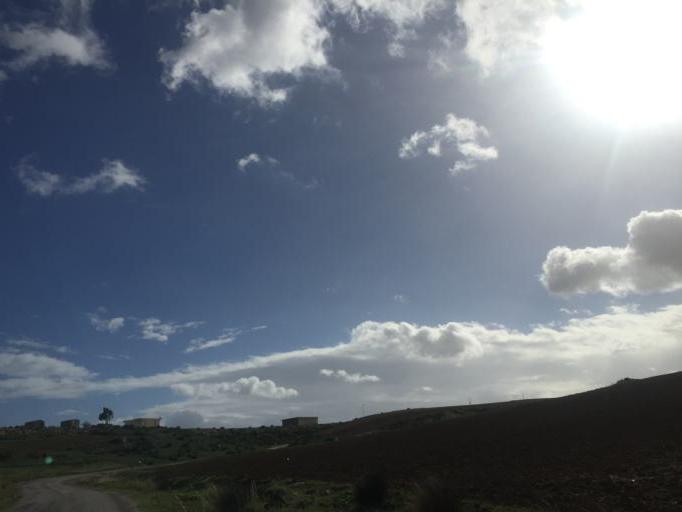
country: TN
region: Nabul
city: El Mida
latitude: 36.8119
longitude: 10.8440
